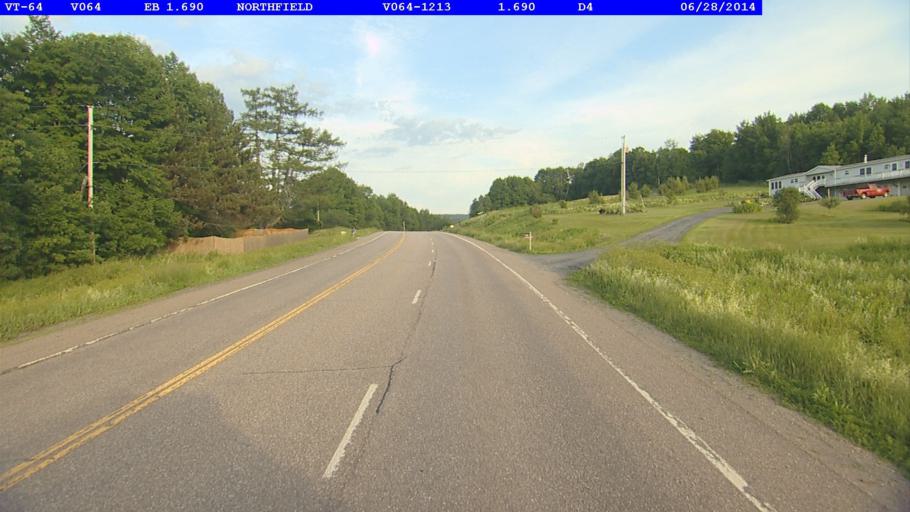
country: US
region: Vermont
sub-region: Washington County
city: Northfield
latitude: 44.1182
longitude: -72.6279
